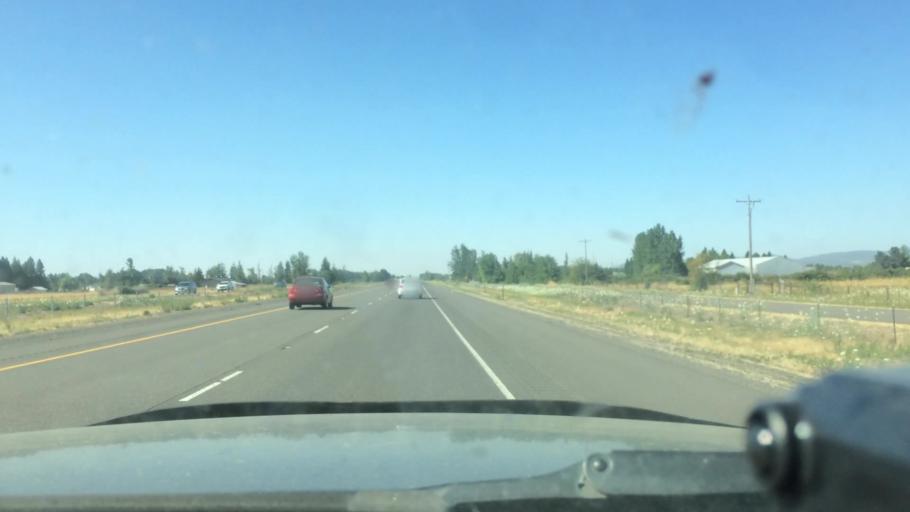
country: US
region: Oregon
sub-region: Lane County
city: Coburg
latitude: 44.2093
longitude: -123.0604
